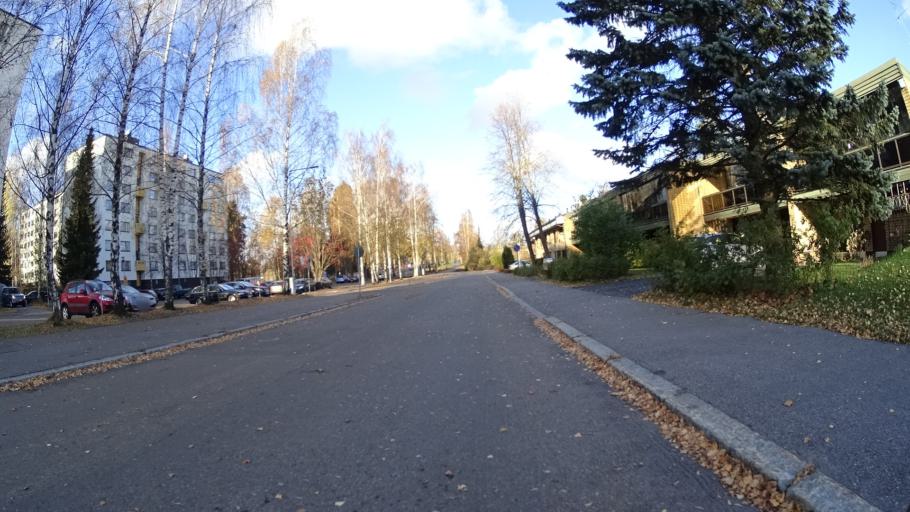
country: FI
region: Uusimaa
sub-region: Helsinki
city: Kilo
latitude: 60.2595
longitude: 24.8303
